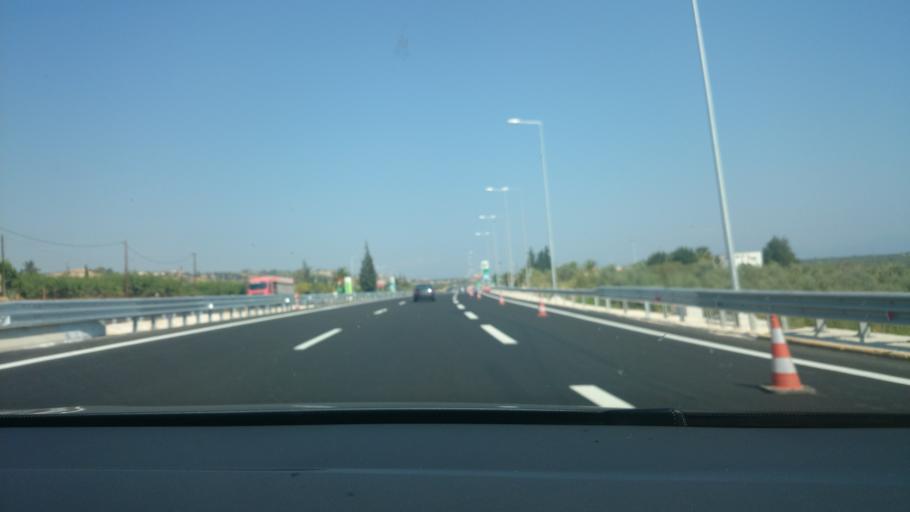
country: GR
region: Peloponnese
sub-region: Nomos Korinthias
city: Velo
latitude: 37.9723
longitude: 22.7431
